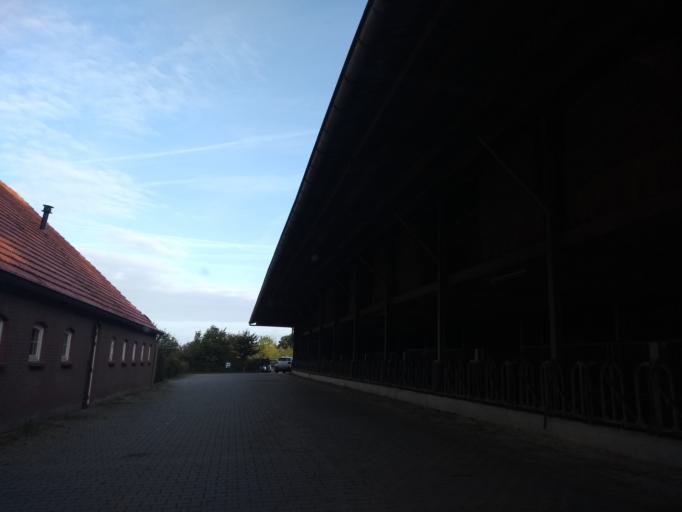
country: DE
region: Lower Saxony
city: Lage
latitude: 52.4184
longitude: 6.9704
